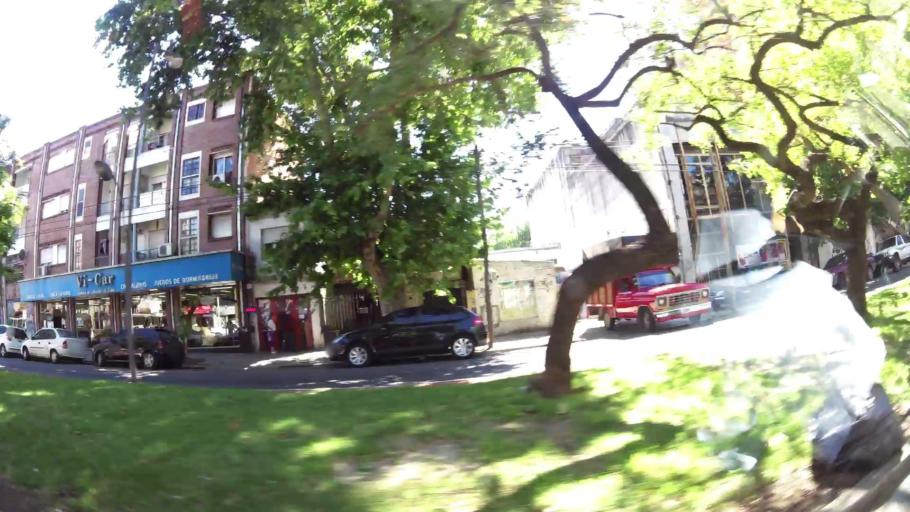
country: AR
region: Buenos Aires
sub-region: Partido de General San Martin
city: General San Martin
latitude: -34.5758
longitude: -58.5323
